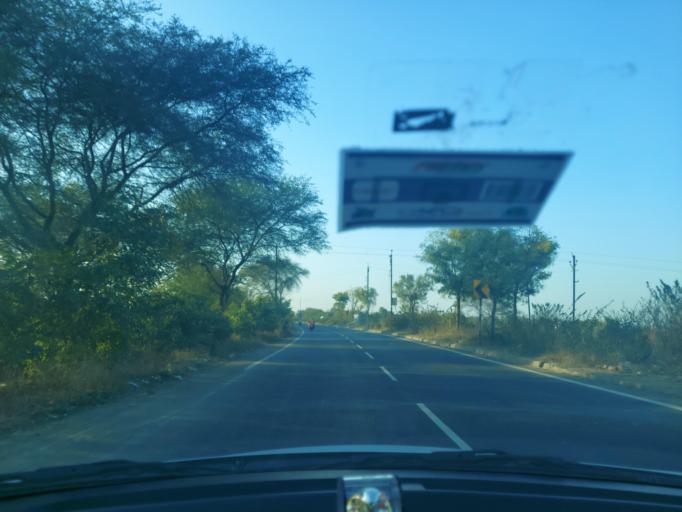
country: IN
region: Madhya Pradesh
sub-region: Indore
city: Sanwer
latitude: 23.0473
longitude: 75.8290
